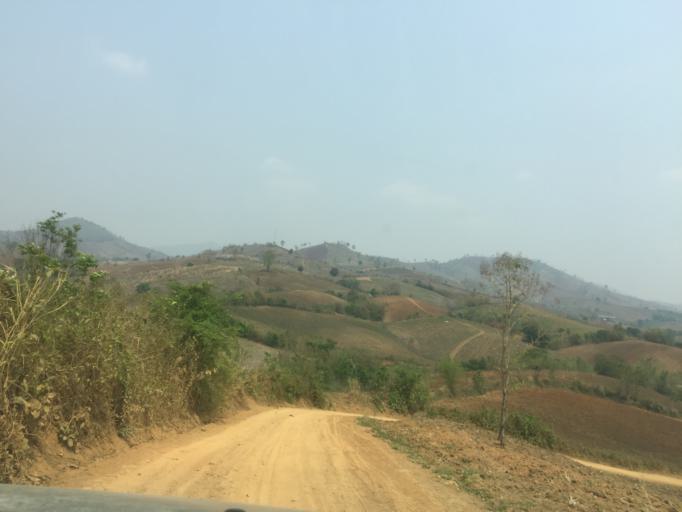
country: LA
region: Xiagnabouli
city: Muang Kenthao
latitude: 17.8006
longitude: 101.2672
